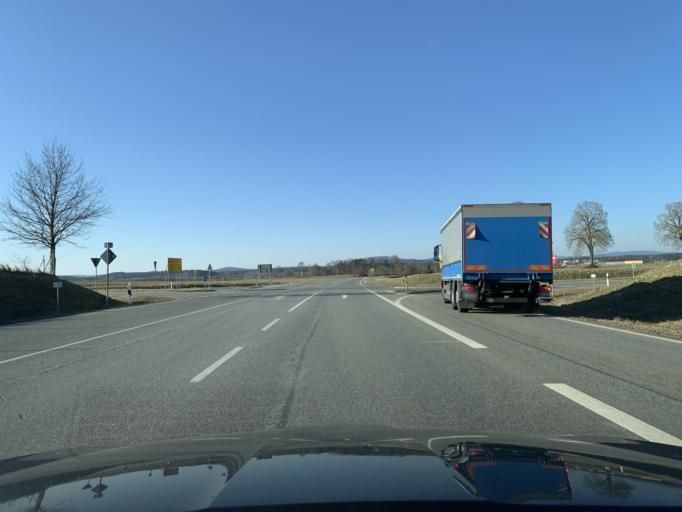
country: DE
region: Bavaria
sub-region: Upper Palatinate
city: Schonthal
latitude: 49.3391
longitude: 12.6074
